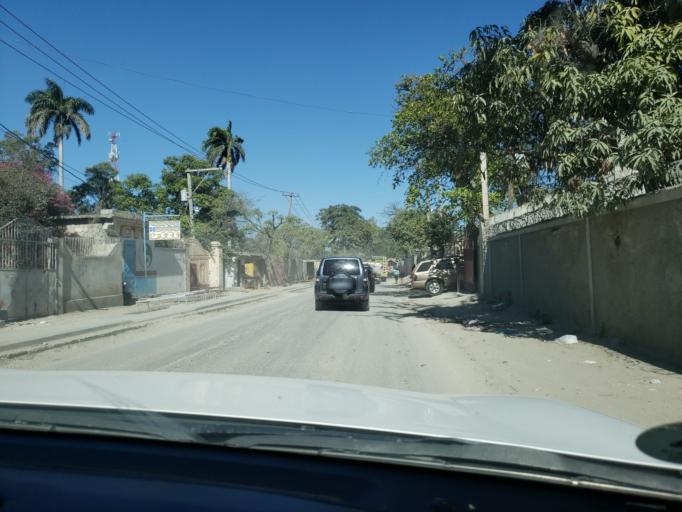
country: HT
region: Ouest
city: Croix des Bouquets
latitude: 18.5743
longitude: -72.2282
